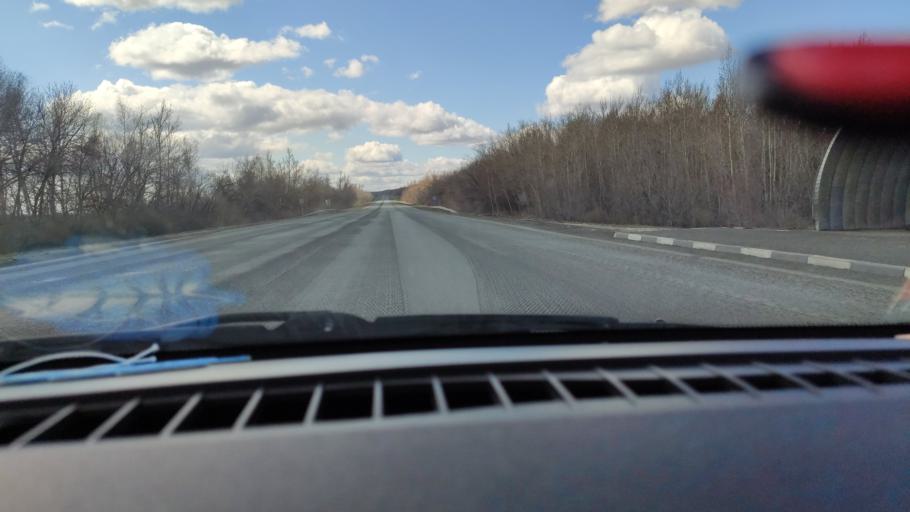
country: RU
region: Saratov
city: Dukhovnitskoye
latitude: 52.6561
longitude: 48.2056
